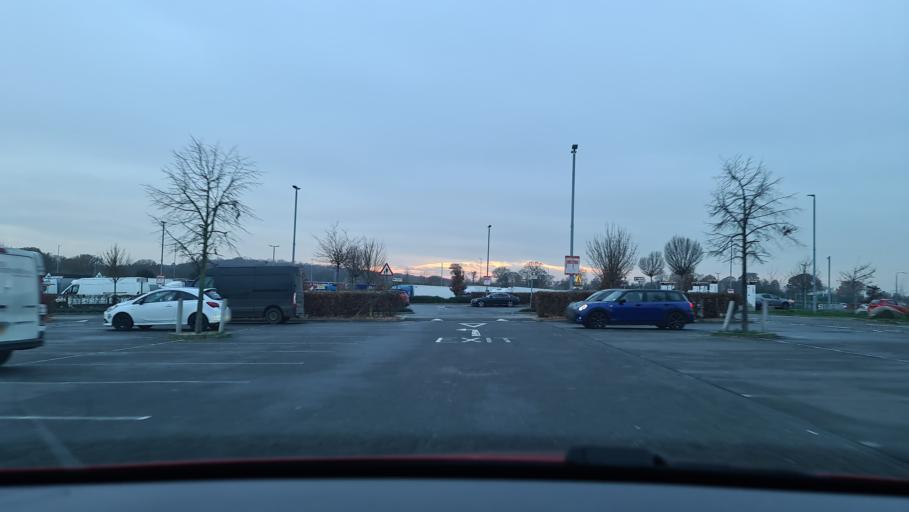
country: GB
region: England
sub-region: Surrey
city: Cobham
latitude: 51.3054
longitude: -0.4057
